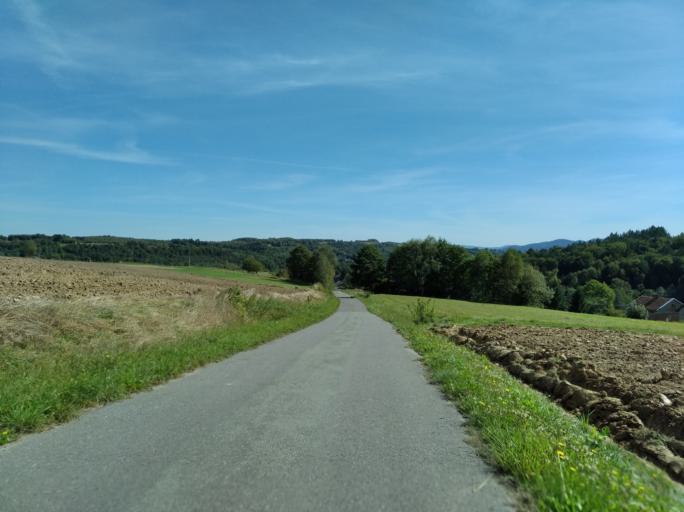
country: PL
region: Subcarpathian Voivodeship
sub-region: Powiat strzyzowski
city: Wisniowa
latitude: 49.8969
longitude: 21.6325
